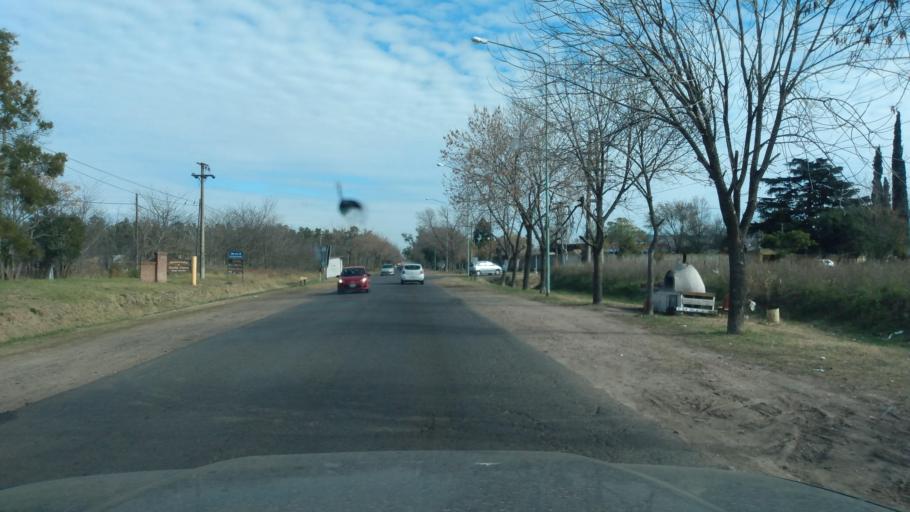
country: AR
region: Buenos Aires
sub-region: Partido de Lujan
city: Lujan
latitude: -34.5785
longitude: -59.1691
